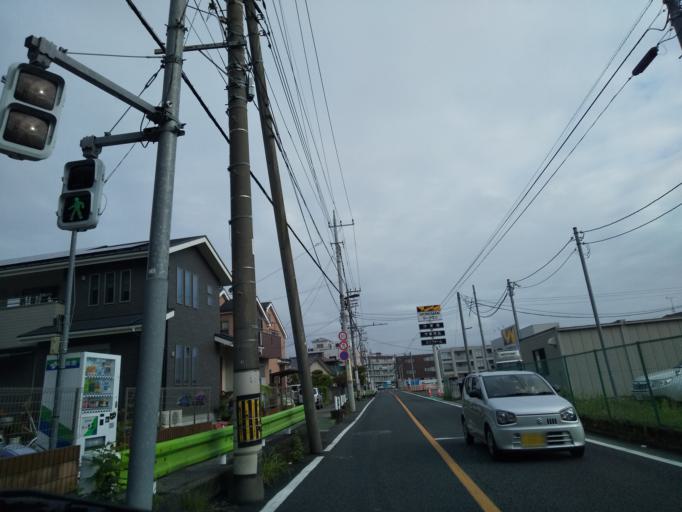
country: JP
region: Tokyo
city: Hino
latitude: 35.6752
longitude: 139.4012
